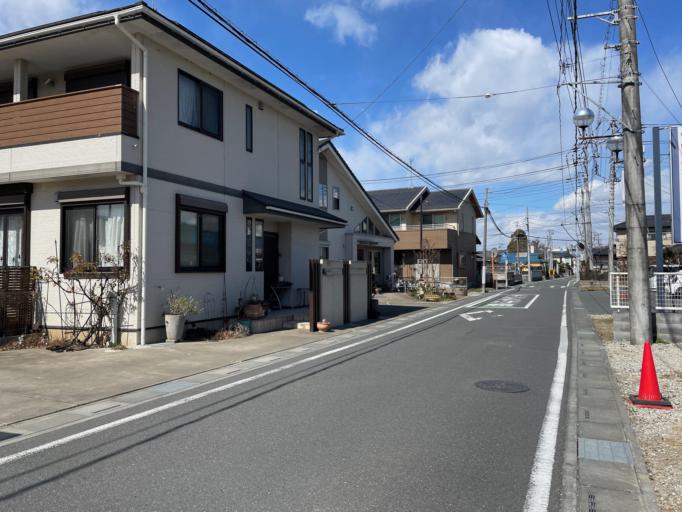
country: JP
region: Saitama
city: Sakado
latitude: 35.9987
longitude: 139.4029
